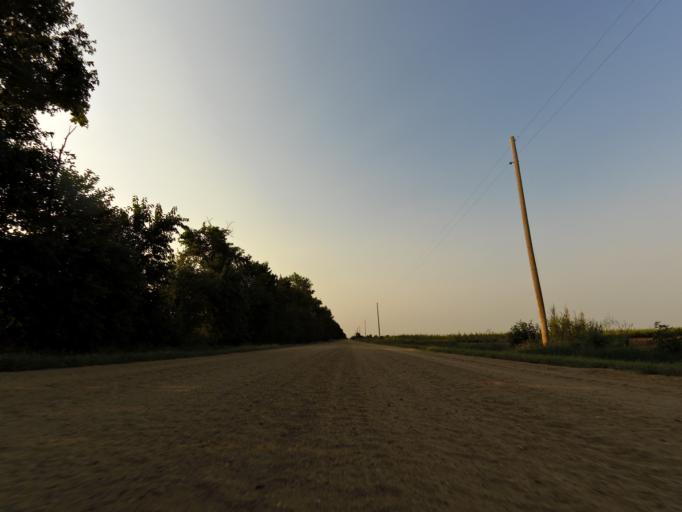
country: US
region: Kansas
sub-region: Reno County
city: South Hutchinson
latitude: 37.9893
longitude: -97.9956
